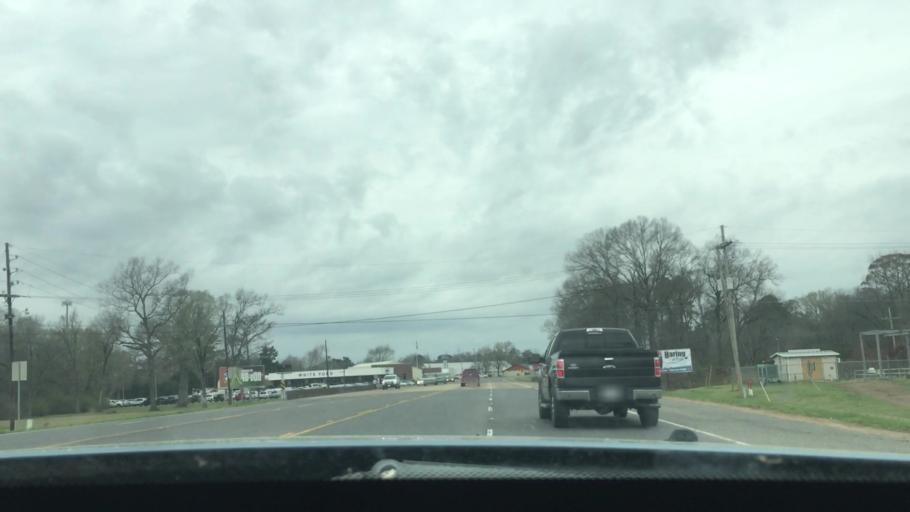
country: US
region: Louisiana
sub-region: Franklin Parish
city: Winnsboro
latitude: 32.1543
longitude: -91.7107
